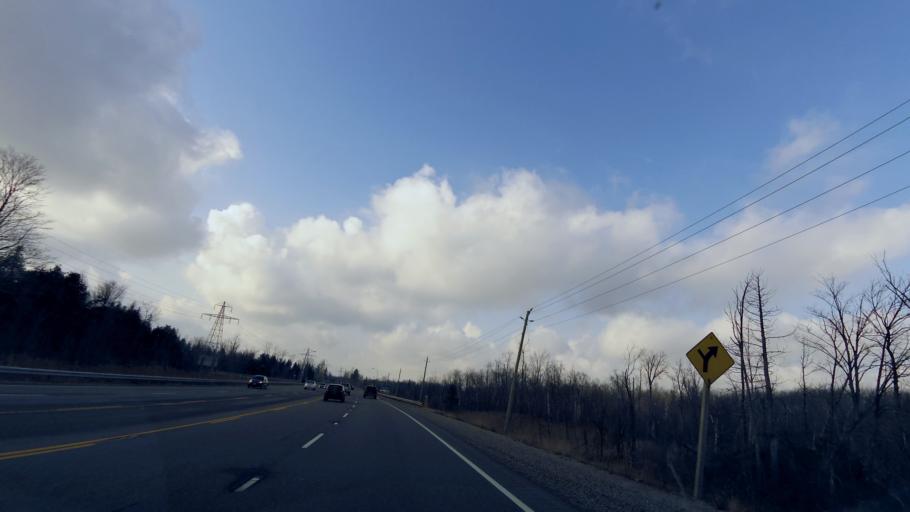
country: CA
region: Ontario
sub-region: Halton
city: Milton
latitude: 43.4098
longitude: -80.0501
